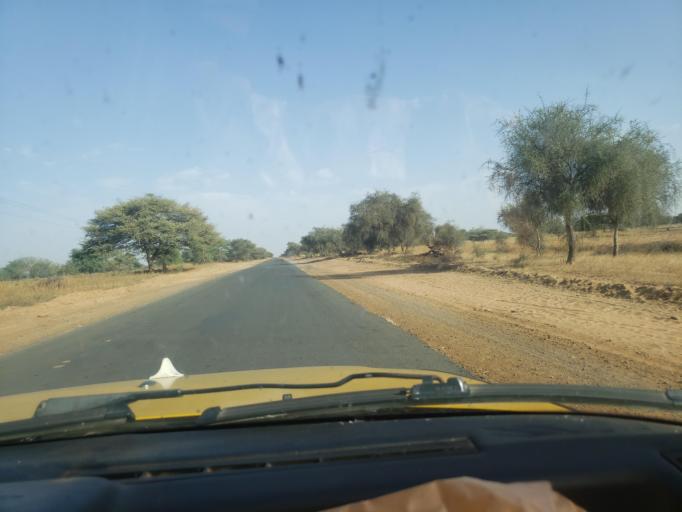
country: SN
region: Louga
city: Louga
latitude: 15.5050
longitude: -15.9571
